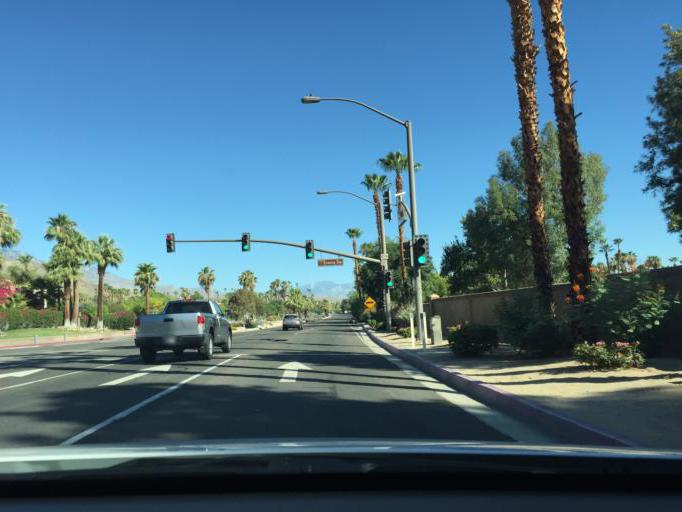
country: US
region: California
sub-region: Riverside County
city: Rancho Mirage
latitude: 33.7515
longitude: -116.4283
